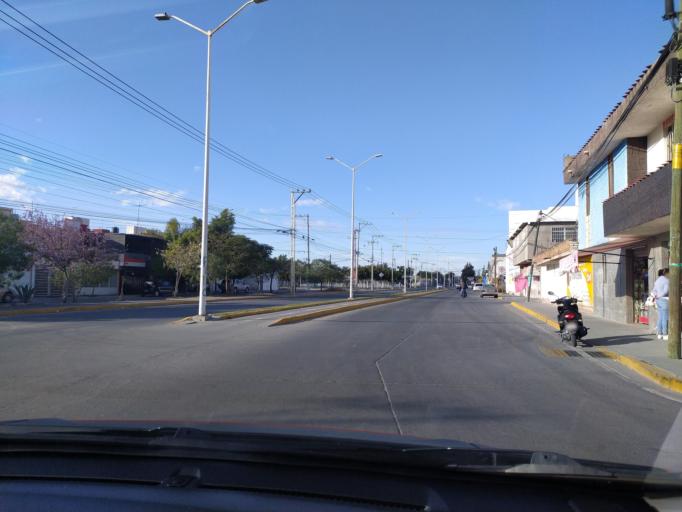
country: MX
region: Guanajuato
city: San Francisco del Rincon
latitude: 21.0204
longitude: -101.8767
